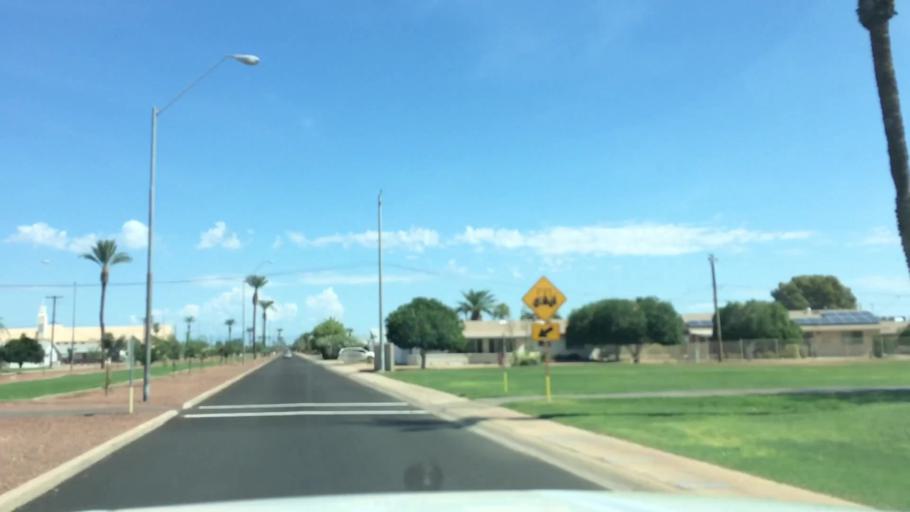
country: US
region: Arizona
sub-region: Maricopa County
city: Youngtown
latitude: 33.5839
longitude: -112.2899
